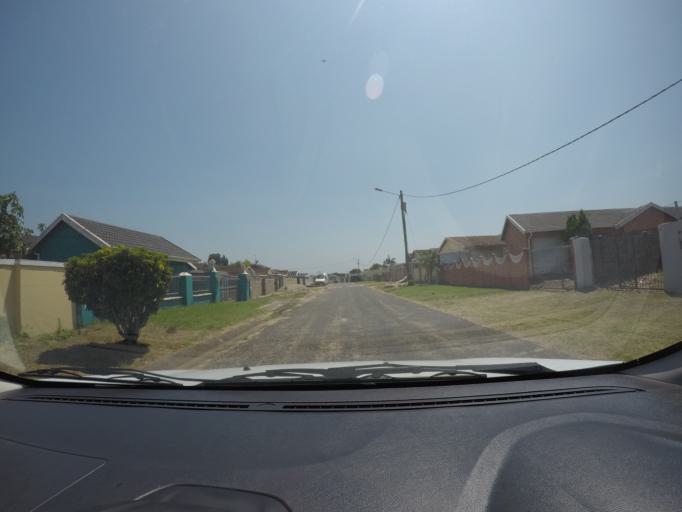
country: ZA
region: KwaZulu-Natal
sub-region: uThungulu District Municipality
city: eSikhawini
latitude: -28.8693
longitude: 31.9221
